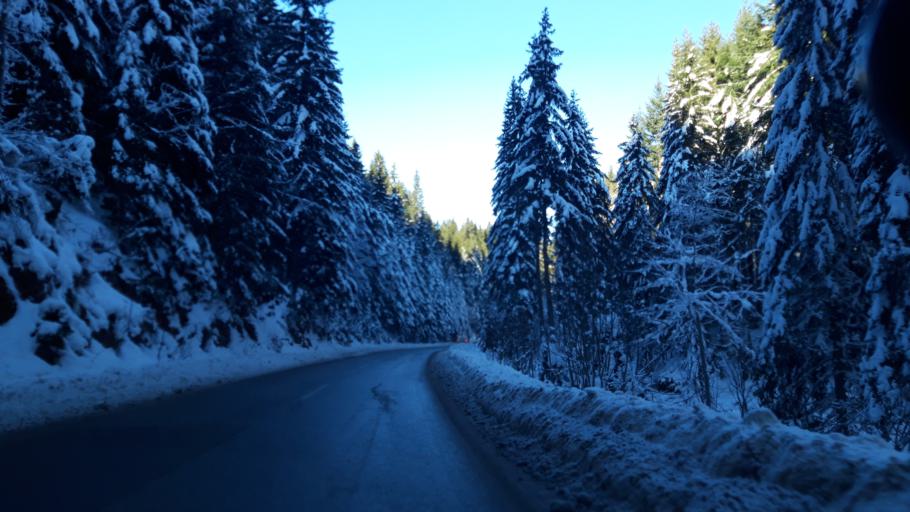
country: BA
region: Republika Srpska
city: Koran
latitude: 43.7491
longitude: 18.5540
